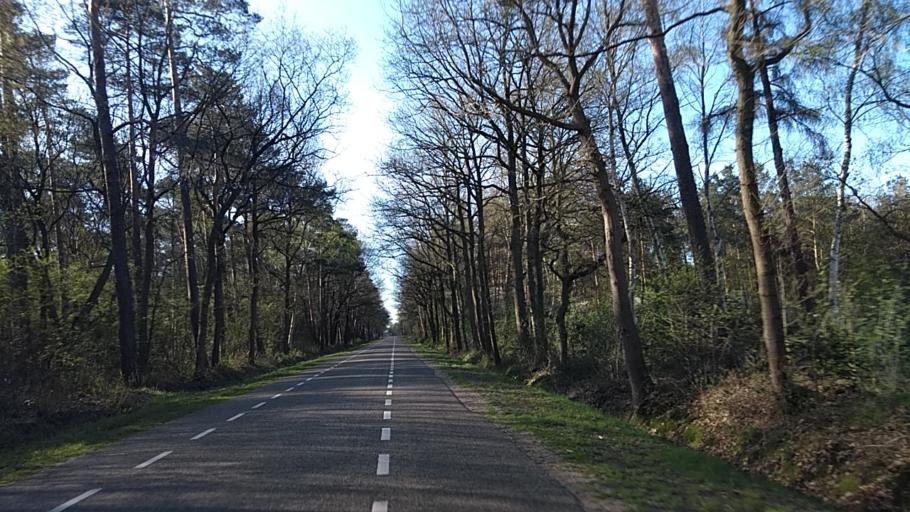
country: NL
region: Overijssel
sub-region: Gemeente Hof van Twente
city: Delden
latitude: 52.2718
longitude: 6.6700
